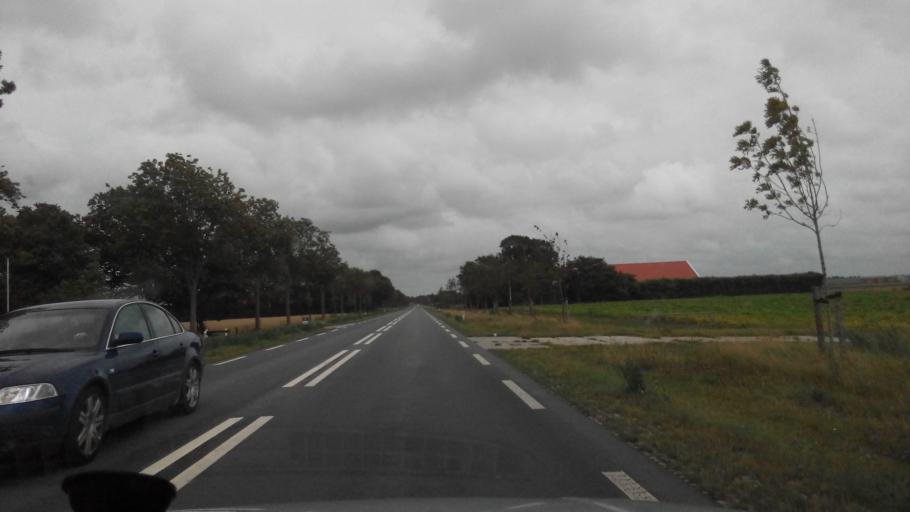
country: NL
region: North Holland
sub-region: Gemeente Hollands Kroon
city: Den Oever
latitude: 52.8440
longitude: 4.9948
